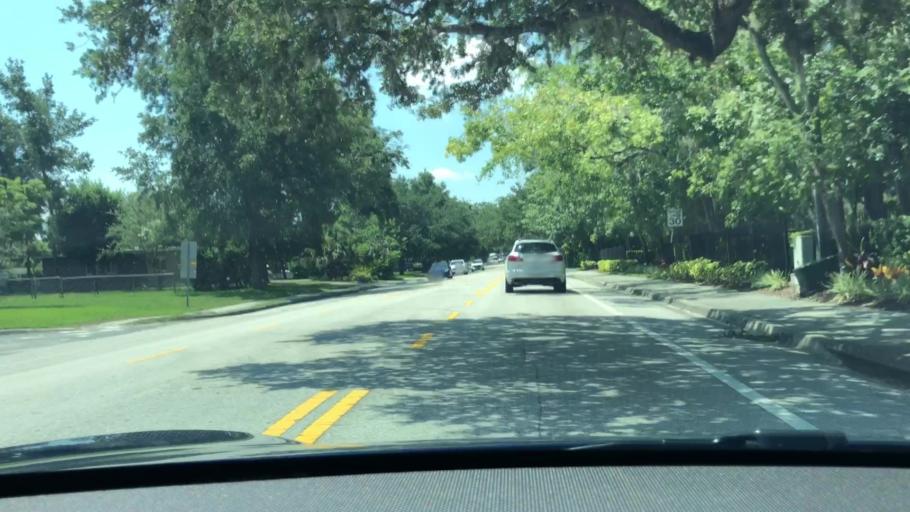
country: US
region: Florida
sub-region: Orange County
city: Winter Park
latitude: 28.5850
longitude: -81.3278
